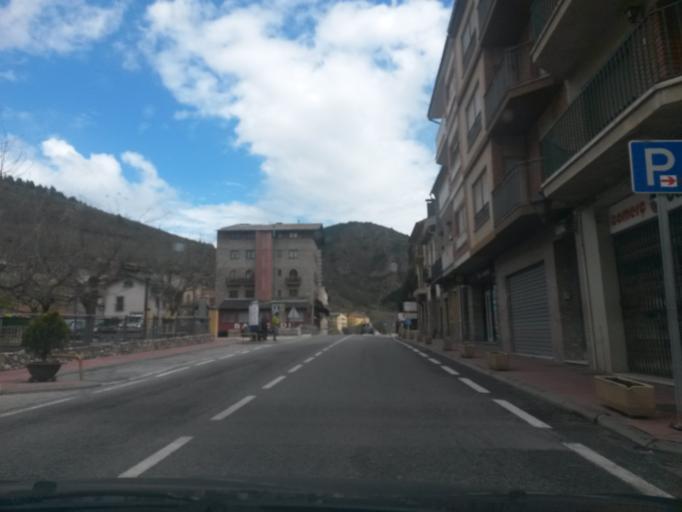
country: ES
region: Catalonia
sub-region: Provincia de Lleida
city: Lles de Cerdanya
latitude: 42.3597
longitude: 1.6950
